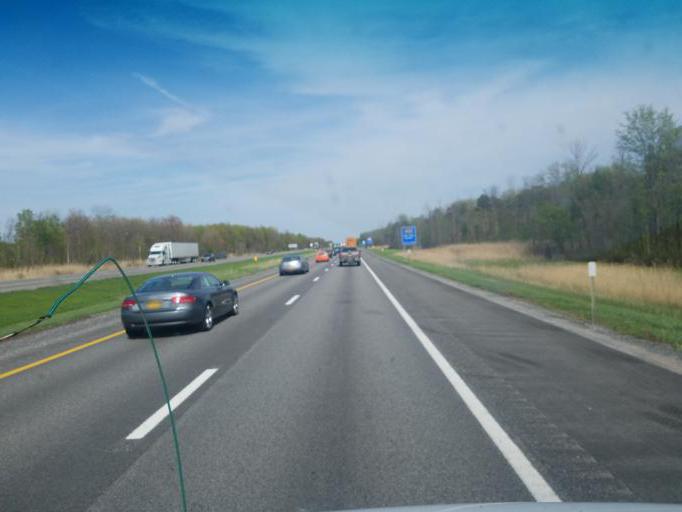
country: US
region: New York
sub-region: Onondaga County
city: Minoa
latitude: 43.0949
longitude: -76.0258
